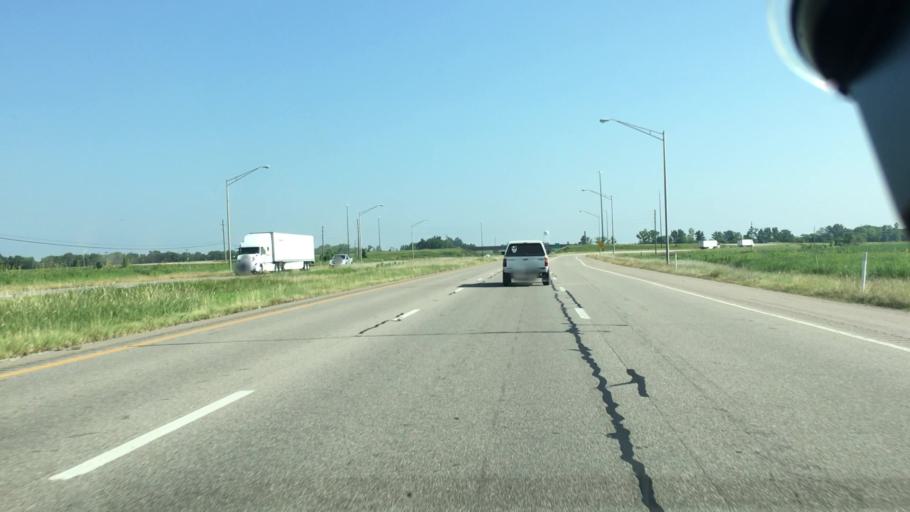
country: US
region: Indiana
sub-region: Gibson County
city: Fort Branch
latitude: 38.2687
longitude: -87.5676
